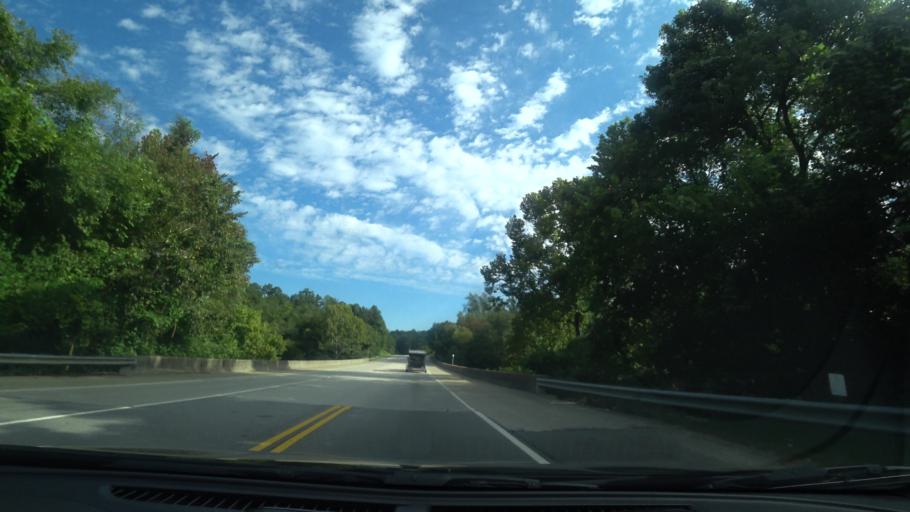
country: US
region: Georgia
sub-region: Rockdale County
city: Conyers
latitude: 33.6918
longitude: -83.9968
